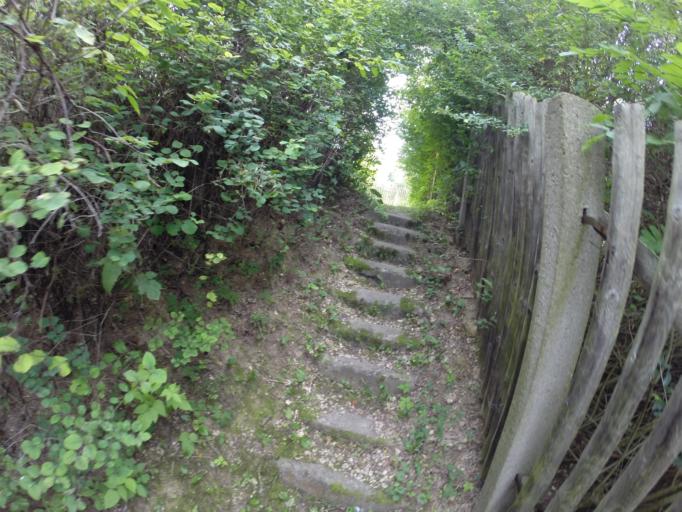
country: DE
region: Thuringia
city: Jena
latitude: 50.9136
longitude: 11.5888
